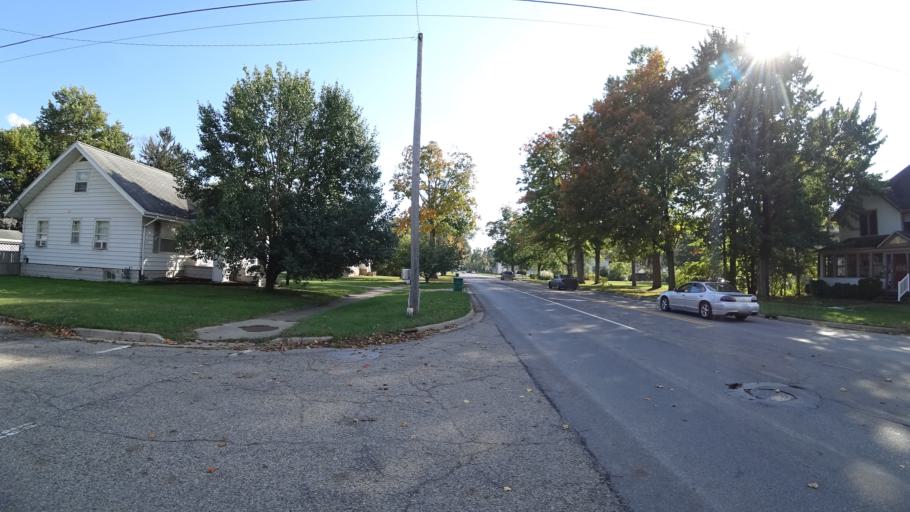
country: US
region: Michigan
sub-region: Saint Joseph County
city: Three Rivers
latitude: 41.9559
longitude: -85.6347
